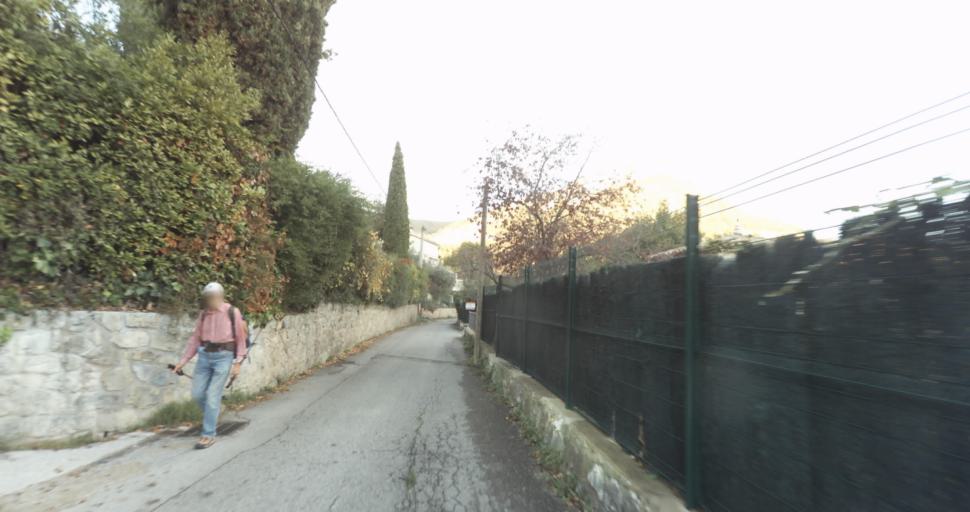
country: FR
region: Provence-Alpes-Cote d'Azur
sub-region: Departement des Alpes-Maritimes
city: Vence
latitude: 43.7300
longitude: 7.1010
